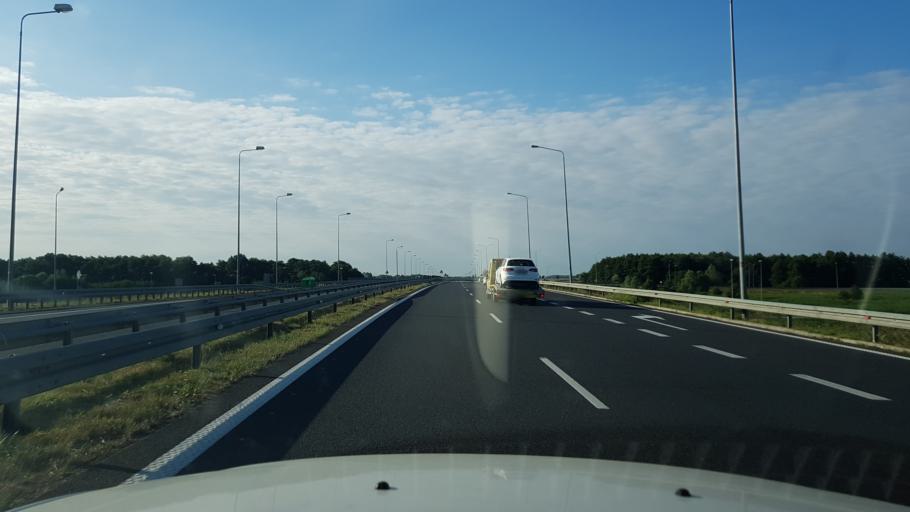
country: PL
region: West Pomeranian Voivodeship
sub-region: Powiat stargardzki
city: Kobylanka
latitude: 53.3499
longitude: 14.9488
